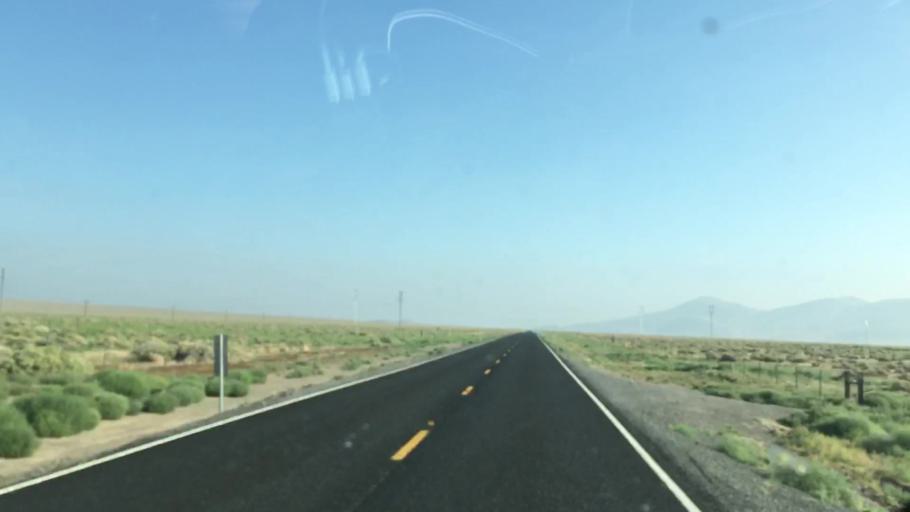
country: US
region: Nevada
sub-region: Lyon County
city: Fernley
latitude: 39.6972
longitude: -119.3349
